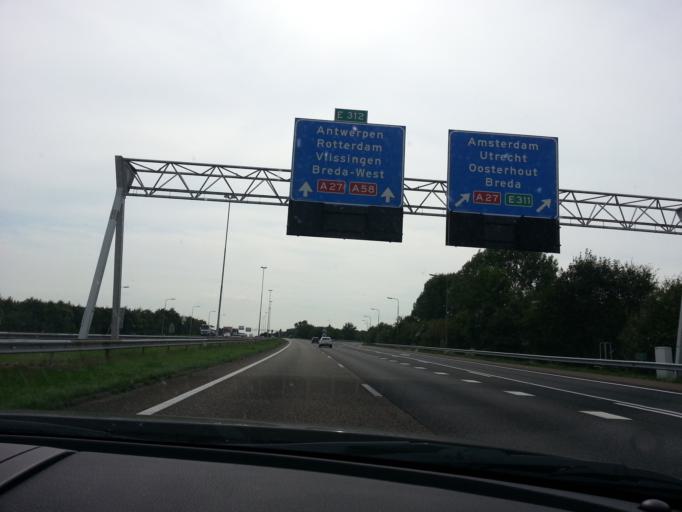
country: NL
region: North Brabant
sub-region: Gemeente Breda
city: Breda
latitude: 51.5531
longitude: 4.8367
